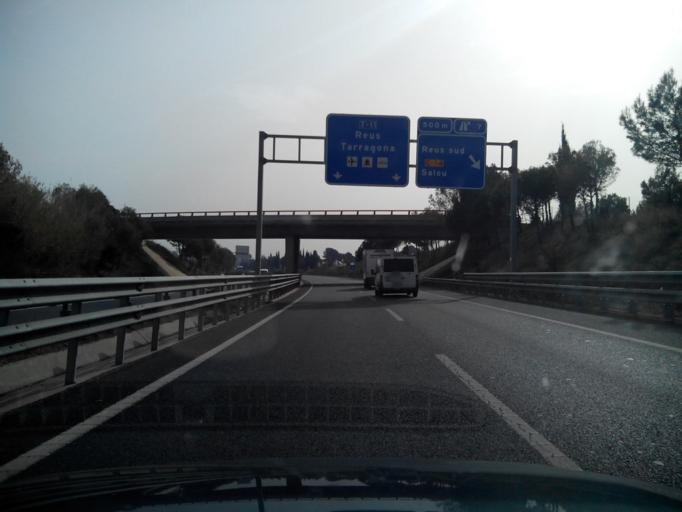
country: ES
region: Catalonia
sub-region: Provincia de Tarragona
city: Reus
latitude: 41.1312
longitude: 1.1078
